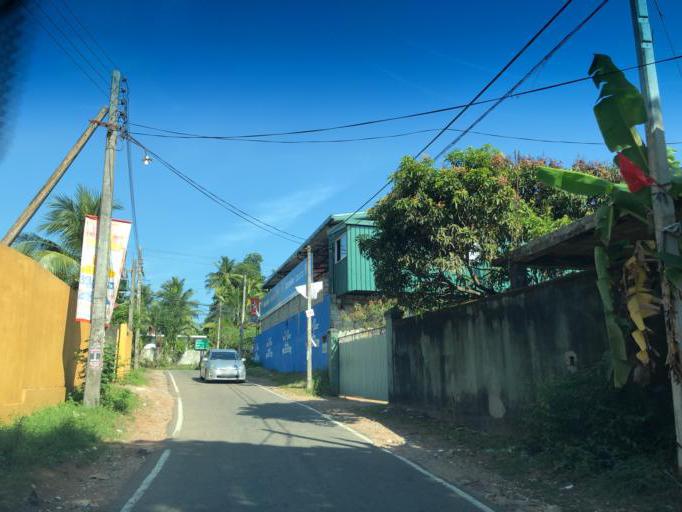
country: LK
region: Western
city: Homagama
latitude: 6.8050
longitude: 79.9785
